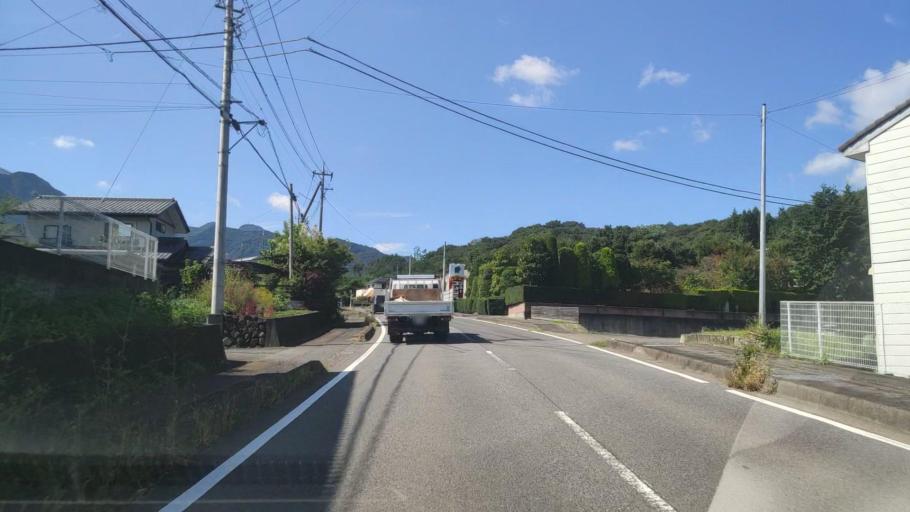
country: JP
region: Gunma
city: Shibukawa
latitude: 36.5010
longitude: 138.9616
